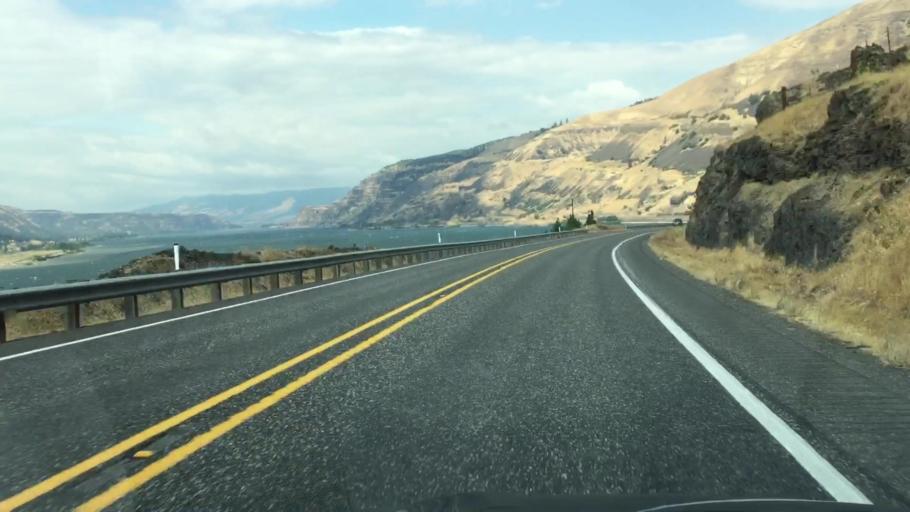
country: US
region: Washington
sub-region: Klickitat County
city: Dallesport
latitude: 45.6635
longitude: -121.2018
